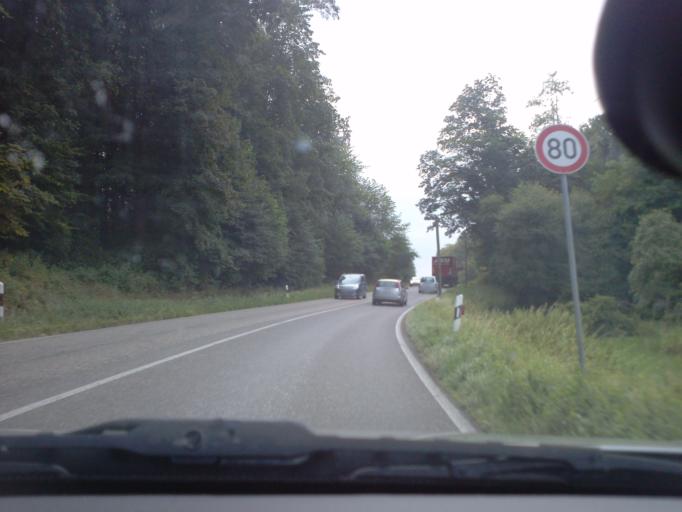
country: DE
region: Baden-Wuerttemberg
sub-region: Karlsruhe Region
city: Joehlingen
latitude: 49.0237
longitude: 8.5638
